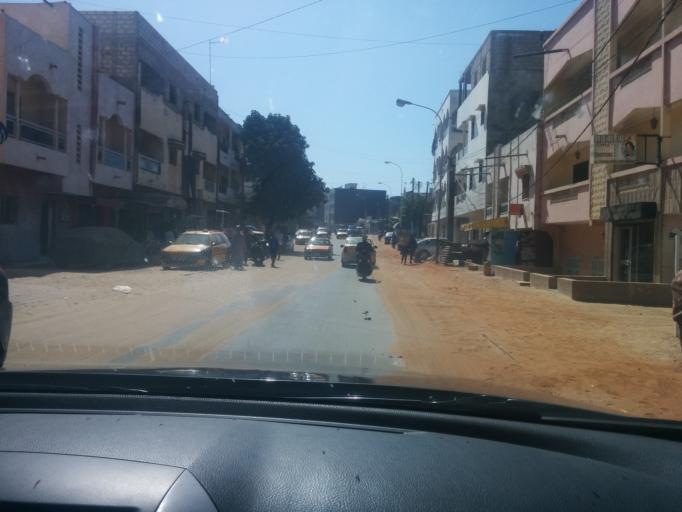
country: SN
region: Dakar
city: Pikine
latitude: 14.7553
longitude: -17.4357
